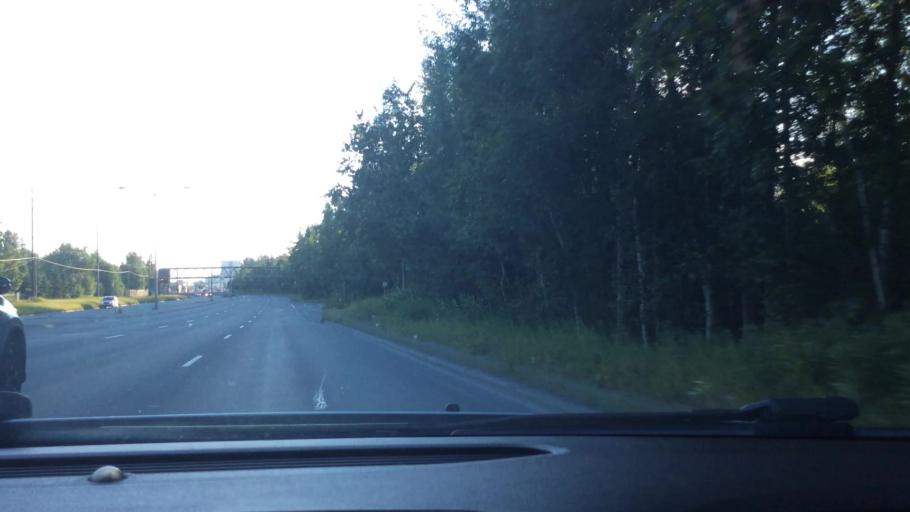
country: US
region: Alaska
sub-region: Anchorage Municipality
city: Anchorage
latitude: 61.1956
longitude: -149.8513
